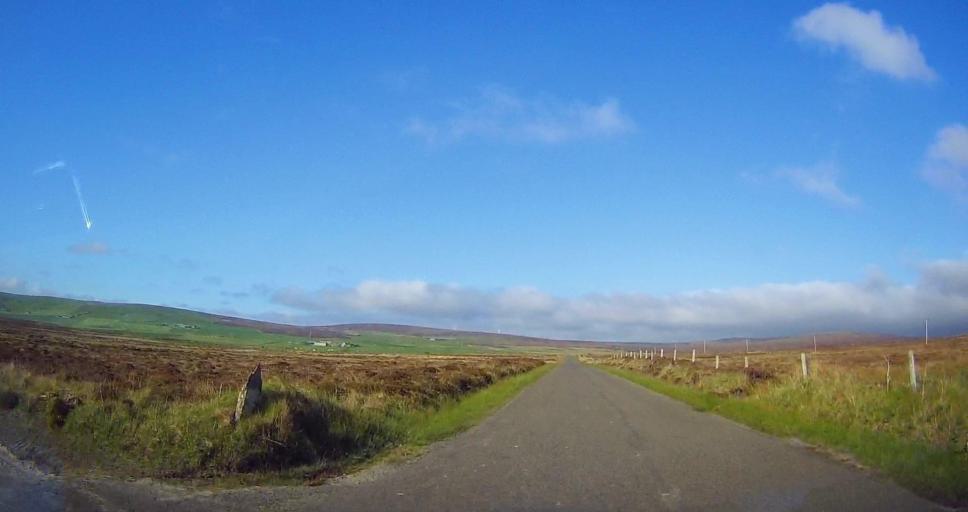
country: GB
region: Scotland
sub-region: Orkney Islands
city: Stromness
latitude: 59.0798
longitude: -3.1974
